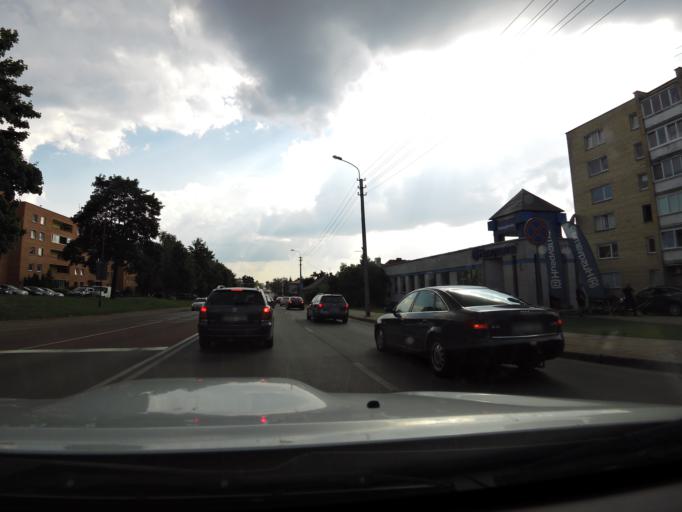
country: LT
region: Siauliu apskritis
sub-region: Siauliai
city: Siauliai
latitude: 55.9331
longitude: 23.3024
